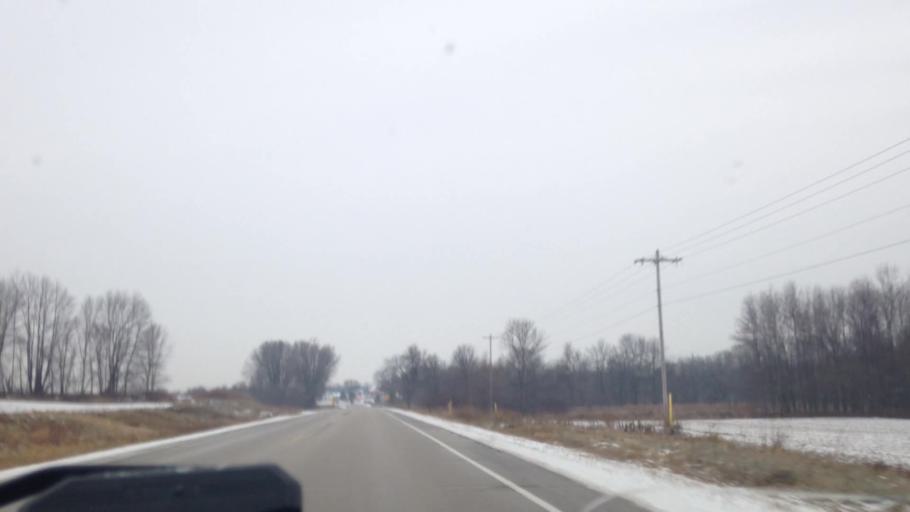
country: US
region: Wisconsin
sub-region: Dodge County
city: Hustisford
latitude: 43.3312
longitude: -88.5162
